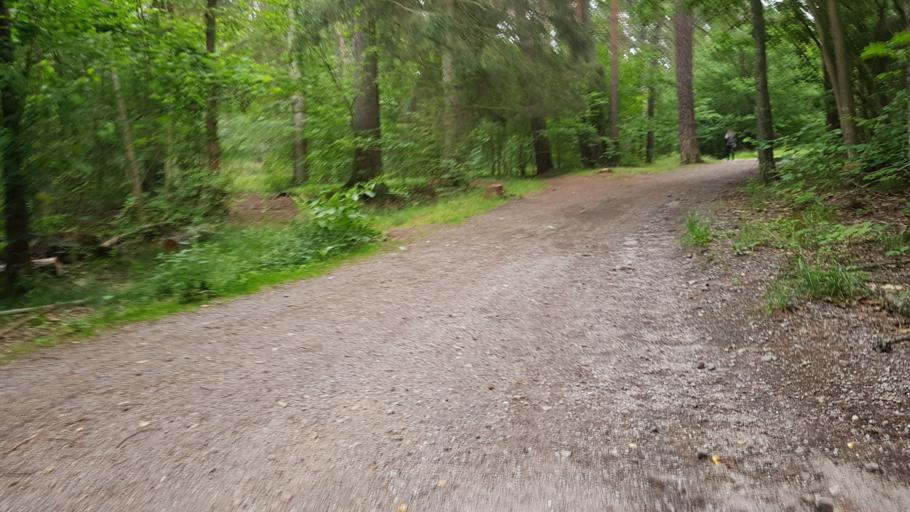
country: SE
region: OEstergoetland
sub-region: Norrkopings Kommun
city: Norrkoping
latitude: 58.5727
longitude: 16.1898
